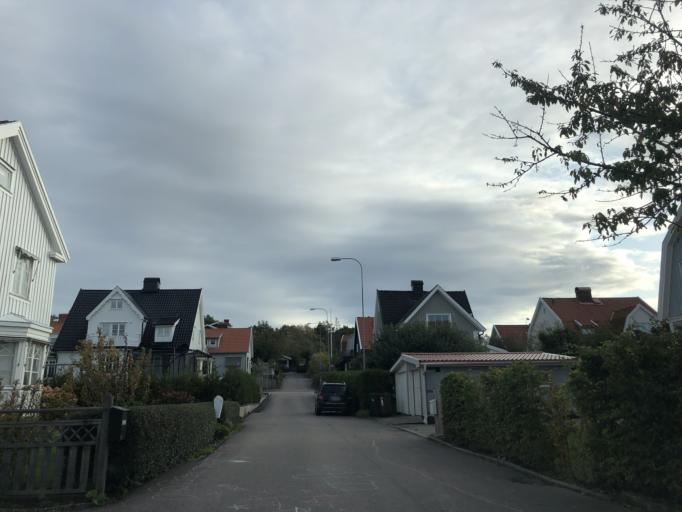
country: SE
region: Vaestra Goetaland
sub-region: Goteborg
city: Majorna
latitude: 57.6694
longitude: 11.8750
